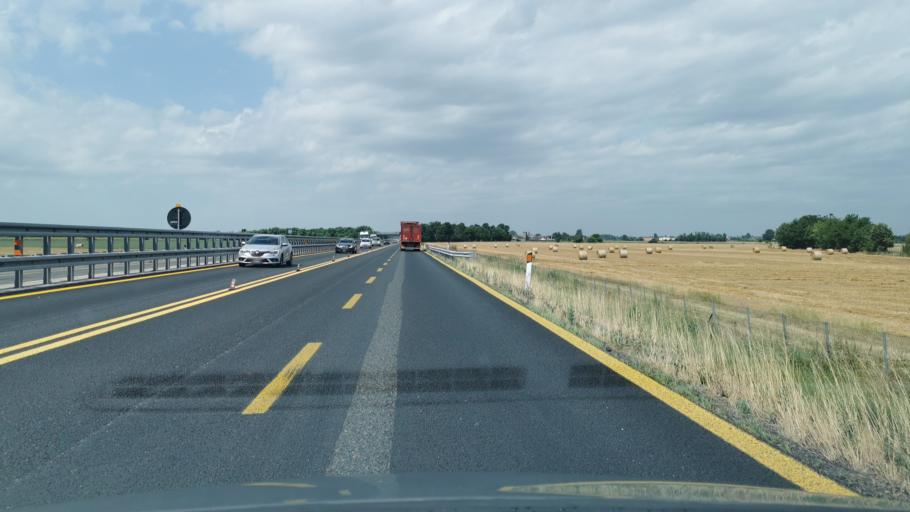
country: IT
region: Lombardy
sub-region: Provincia di Pavia
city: Verretto
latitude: 45.0316
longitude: 9.1063
